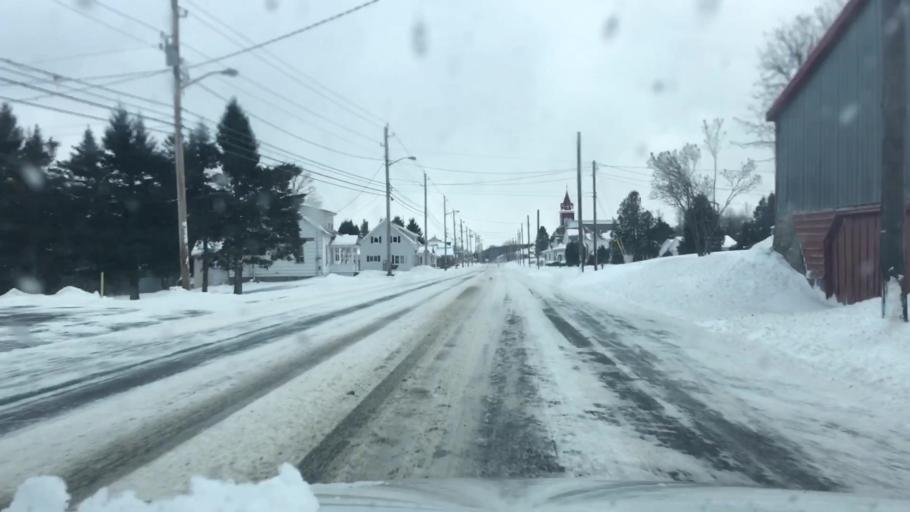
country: US
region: Maine
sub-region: Aroostook County
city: Madawaska
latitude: 47.3105
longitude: -68.1579
